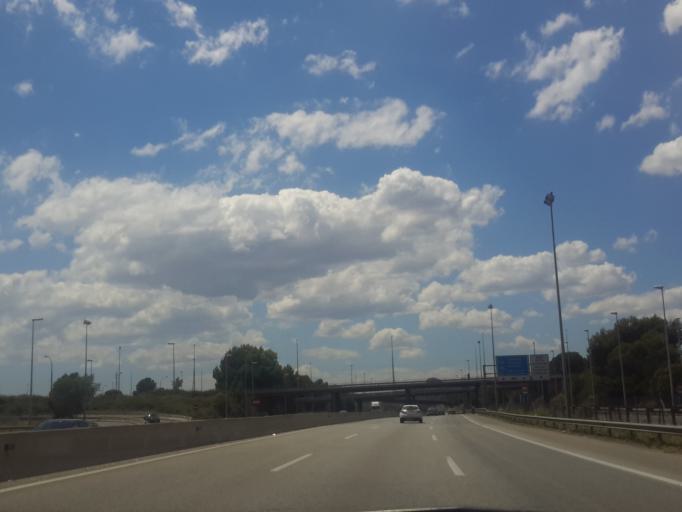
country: ES
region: Catalonia
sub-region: Provincia de Barcelona
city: Barbera del Valles
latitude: 41.5095
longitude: 2.1356
